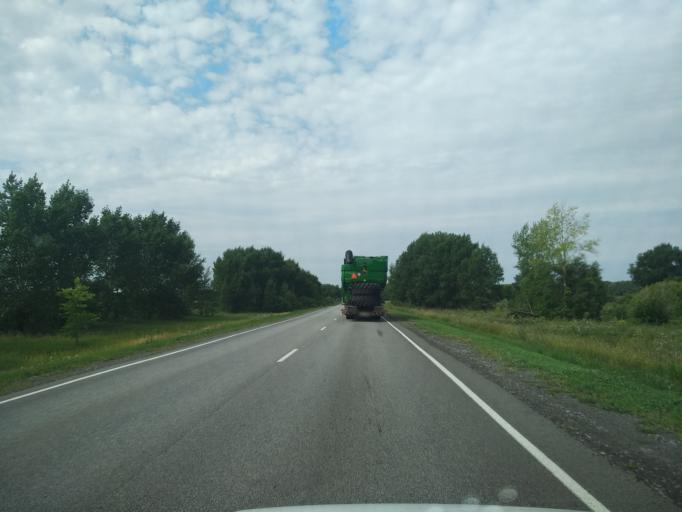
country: RU
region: Voronezj
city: Pereleshinskiy
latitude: 51.8704
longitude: 40.3878
